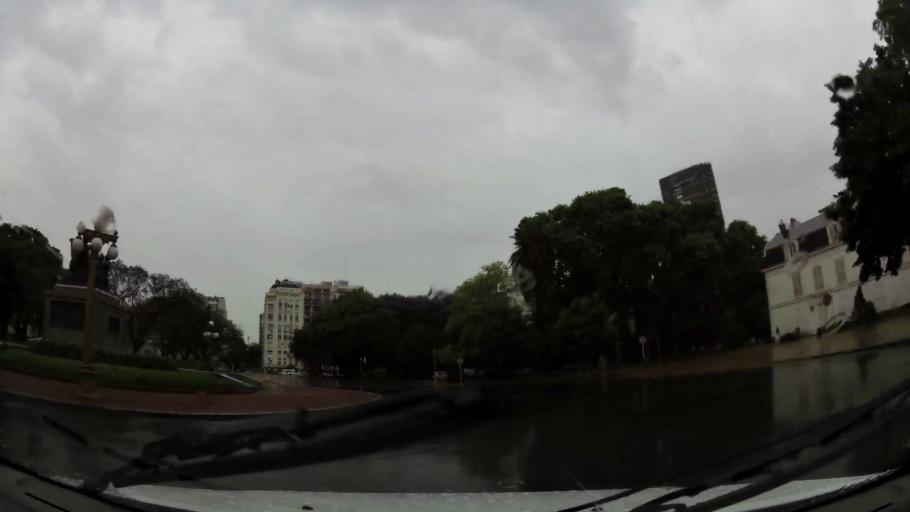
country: AR
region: Buenos Aires F.D.
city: Retiro
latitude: -34.5805
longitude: -58.4011
